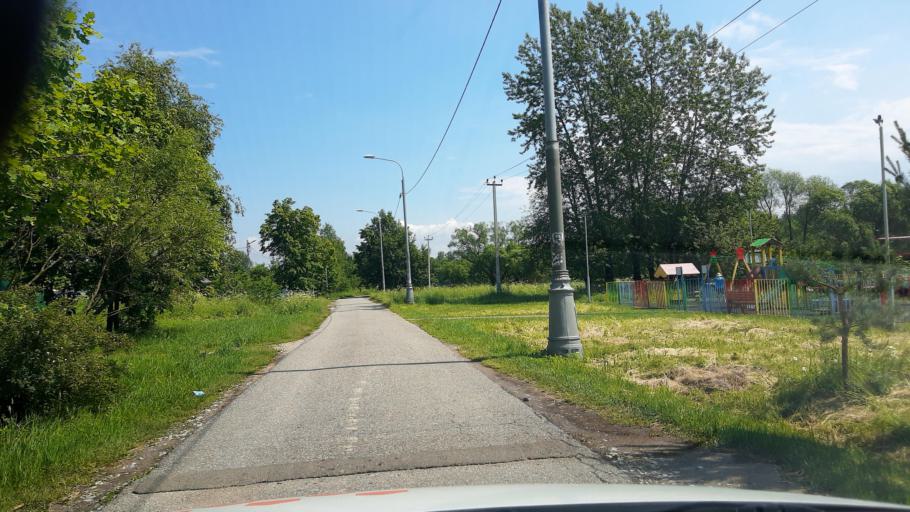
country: RU
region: Moskovskaya
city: Aprelevka
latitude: 55.2895
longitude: 37.1217
